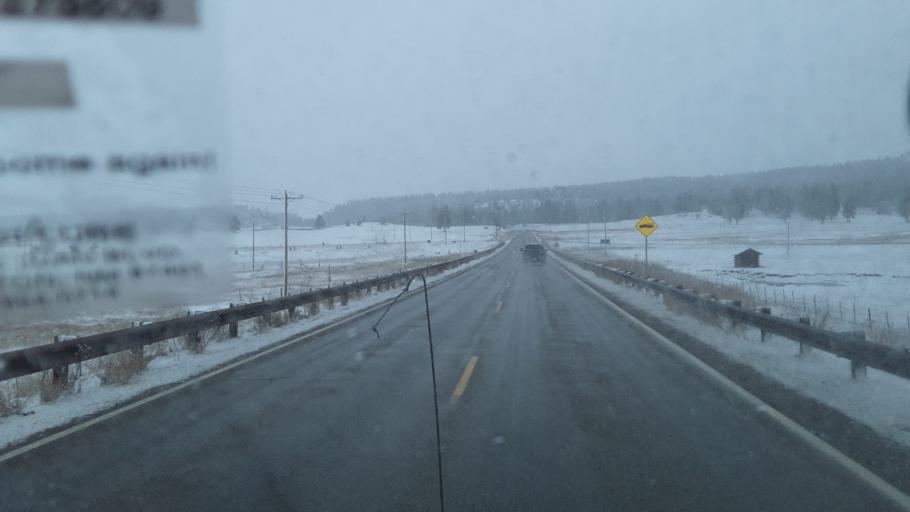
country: US
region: Colorado
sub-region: Archuleta County
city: Pagosa Springs
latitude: 37.1976
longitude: -106.9594
